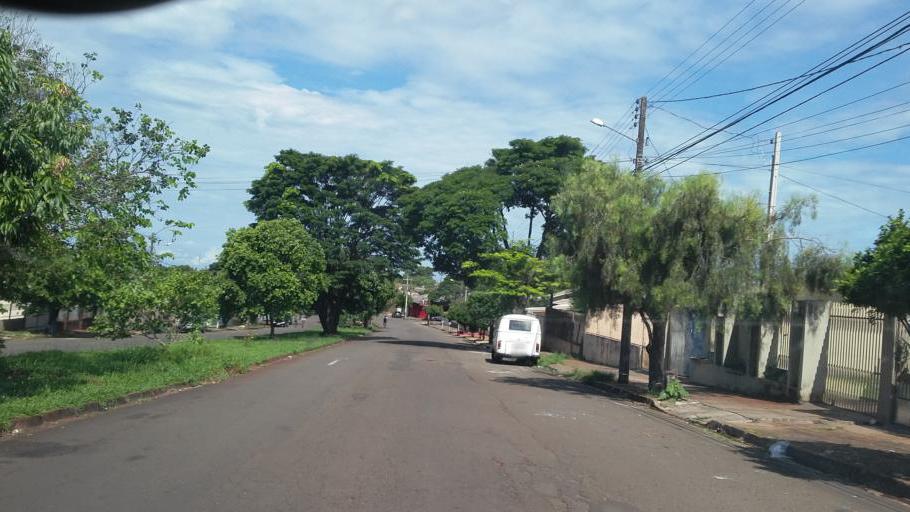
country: BR
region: Parana
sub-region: Londrina
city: Londrina
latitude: -23.2848
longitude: -51.2045
